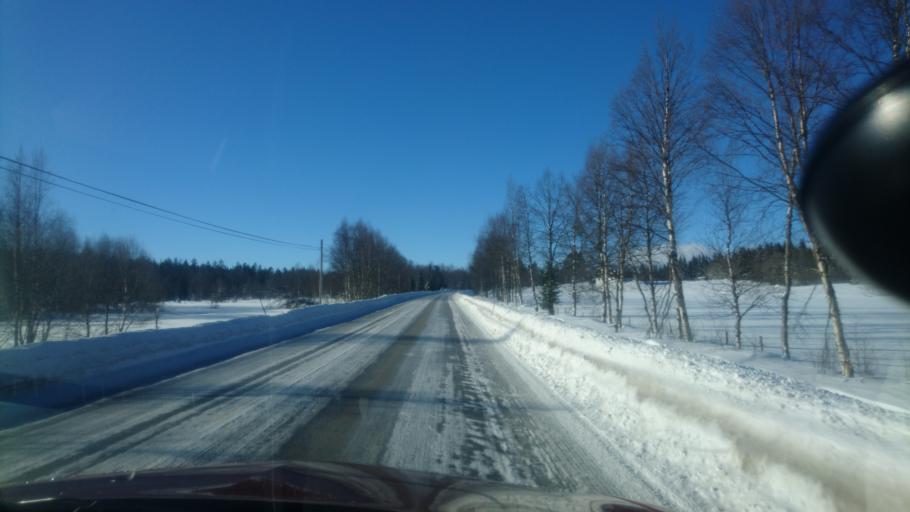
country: NO
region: Hedmark
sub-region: Trysil
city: Innbygda
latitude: 61.2654
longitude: 12.4374
